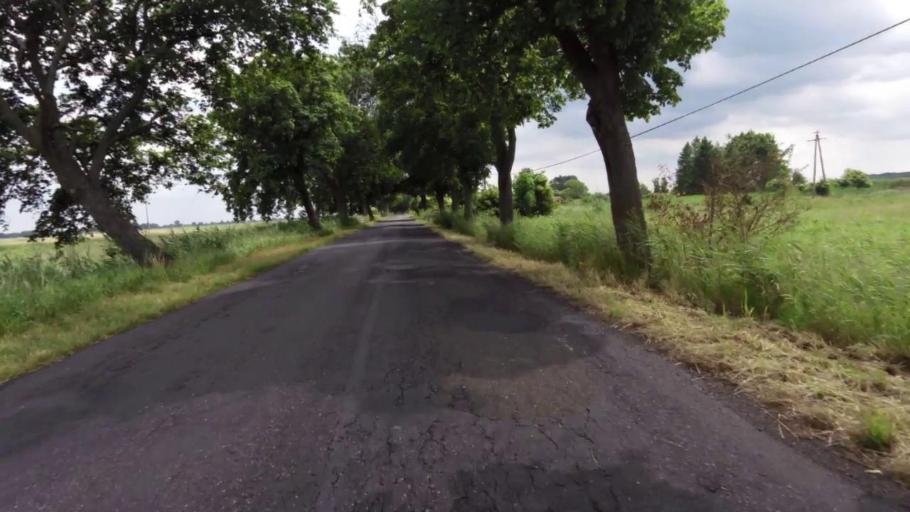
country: PL
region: West Pomeranian Voivodeship
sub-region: Powiat goleniowski
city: Stepnica
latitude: 53.6899
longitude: 14.5485
